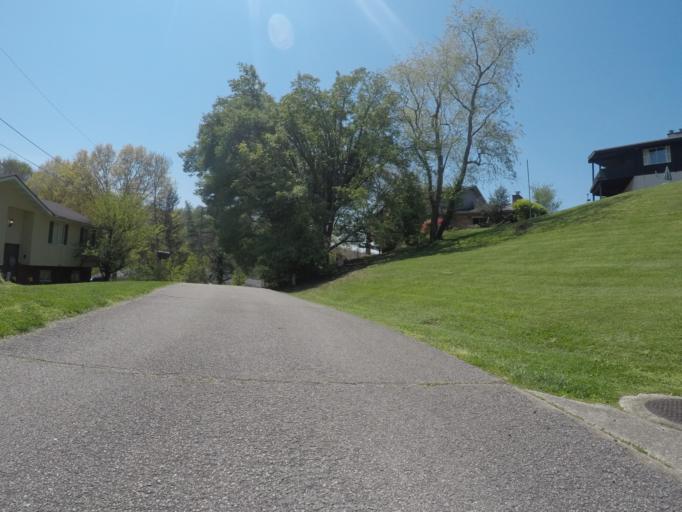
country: US
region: West Virginia
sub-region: Cabell County
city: Pea Ridge
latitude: 38.4088
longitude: -82.3398
